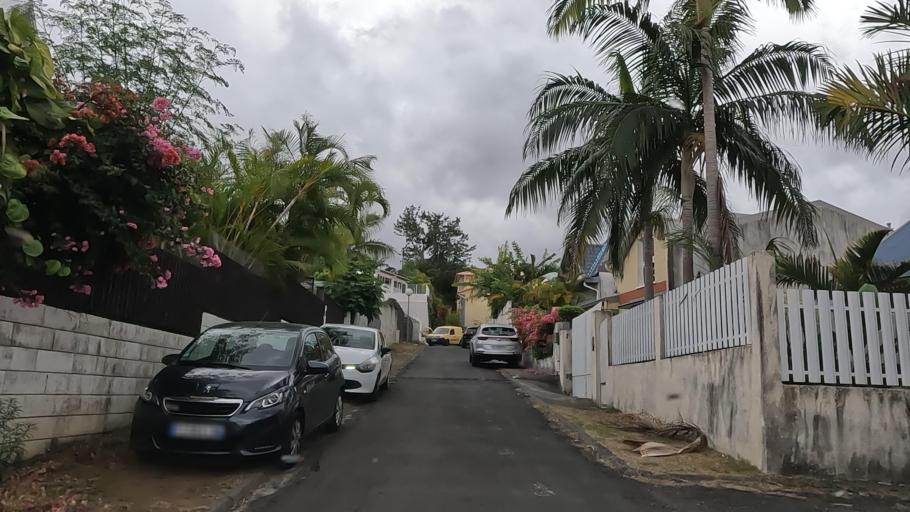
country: RE
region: Reunion
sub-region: Reunion
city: Le Tampon
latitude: -21.2745
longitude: 55.5021
